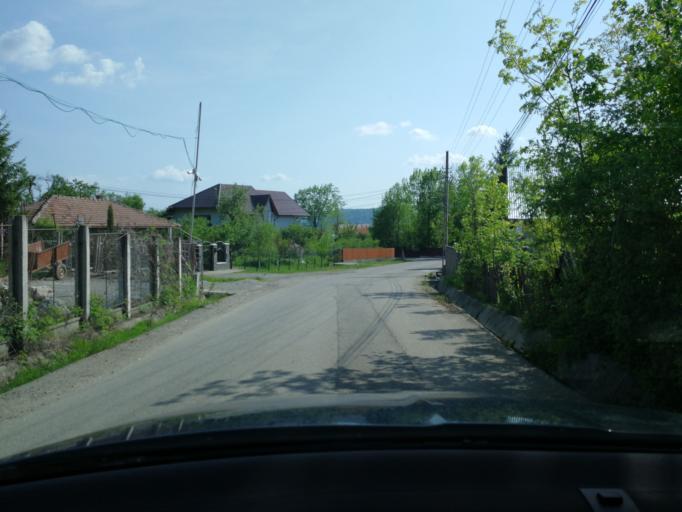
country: RO
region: Prahova
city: Cornu de Sus
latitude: 45.1651
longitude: 25.7045
